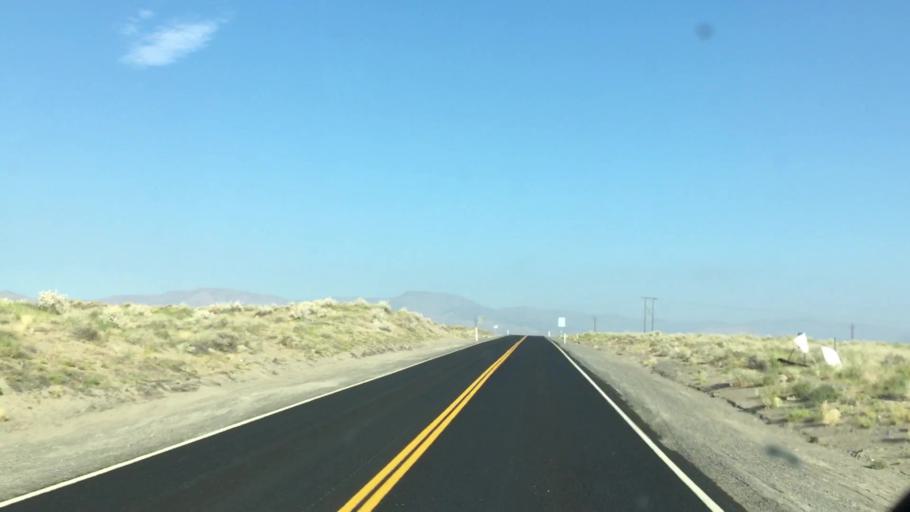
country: US
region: Nevada
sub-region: Lyon County
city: Fernley
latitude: 39.6398
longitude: -119.2957
